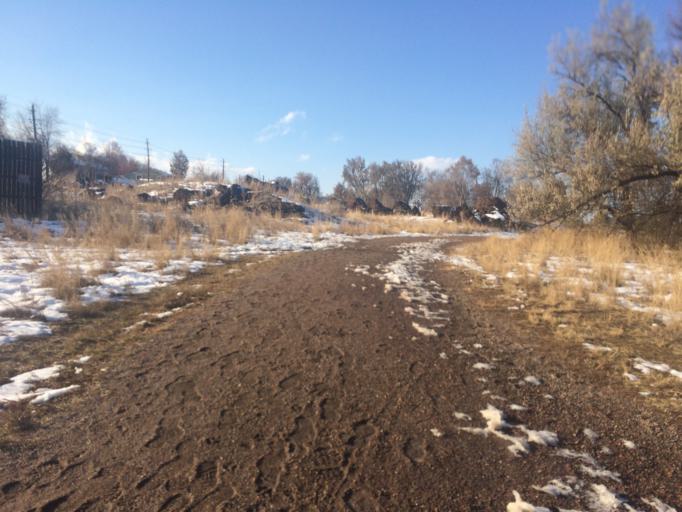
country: US
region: Colorado
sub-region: Boulder County
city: Lafayette
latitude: 39.9911
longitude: -105.1126
